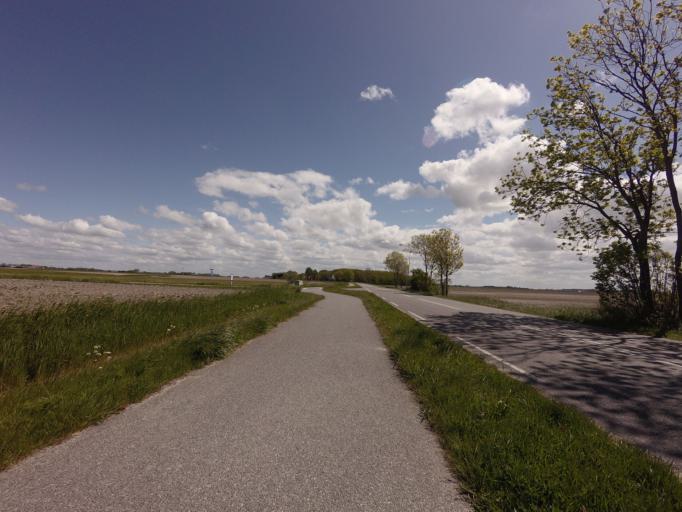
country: NL
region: Friesland
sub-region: Gemeente Harlingen
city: Harlingen
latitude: 53.1387
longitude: 5.4479
